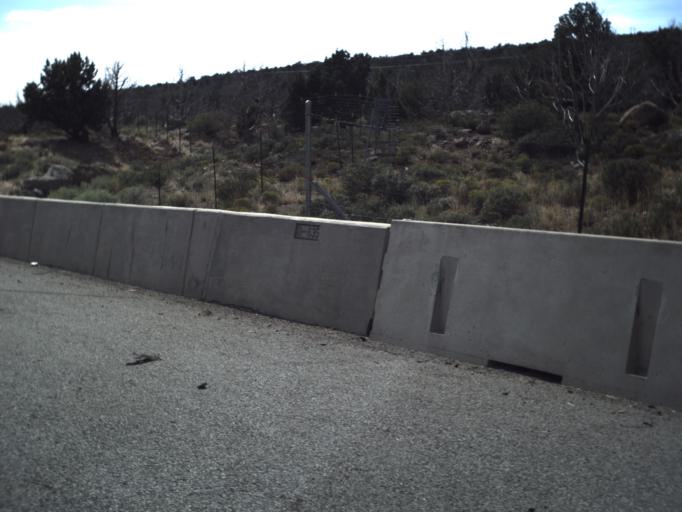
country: US
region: Utah
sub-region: Washington County
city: Toquerville
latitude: 37.3587
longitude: -113.2642
